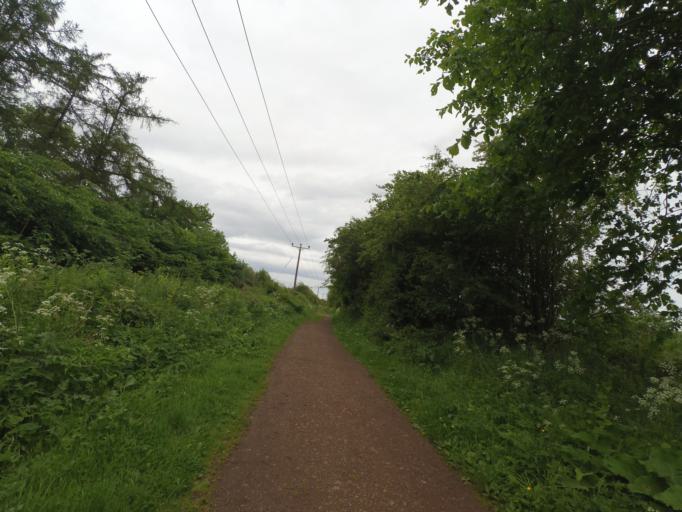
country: GB
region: Scotland
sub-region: East Lothian
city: Macmerry
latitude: 55.9282
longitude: -2.9100
